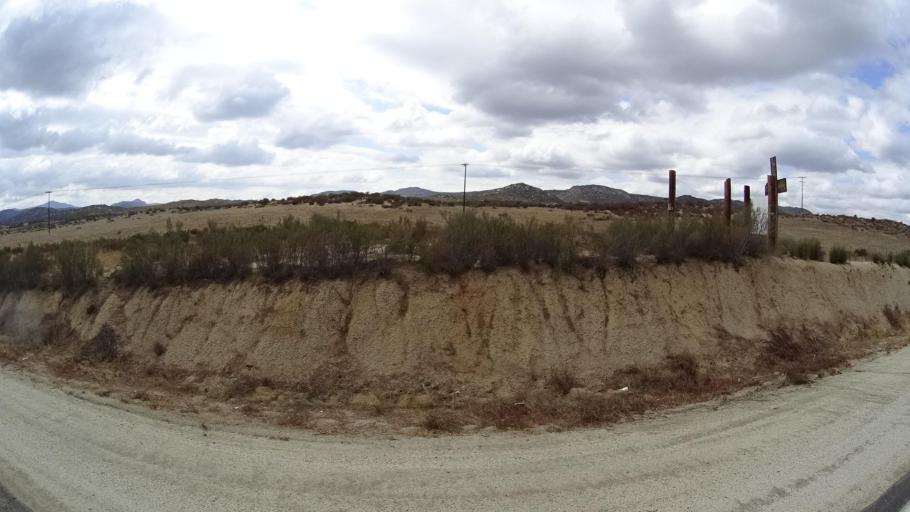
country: US
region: California
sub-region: San Diego County
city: Campo
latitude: 32.6380
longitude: -116.4796
